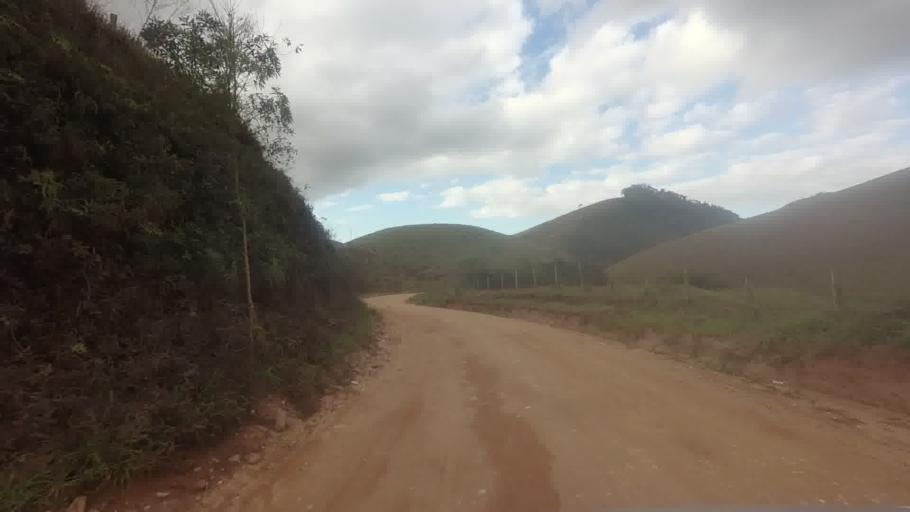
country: BR
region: Espirito Santo
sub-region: Mimoso Do Sul
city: Mimoso do Sul
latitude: -20.9492
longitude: -41.4164
